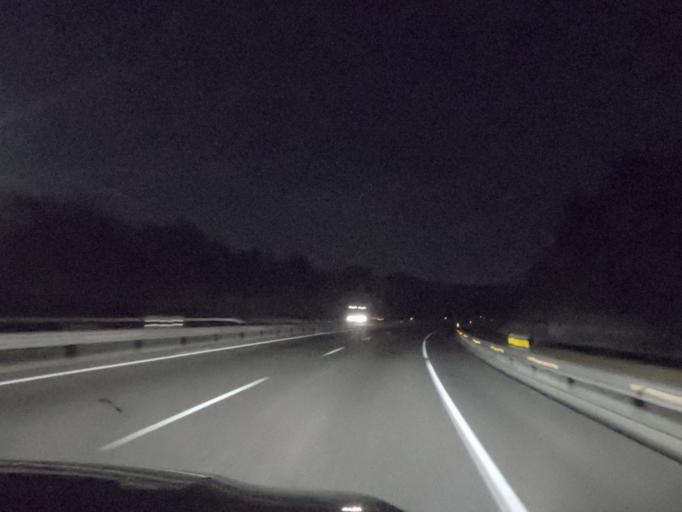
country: ES
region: Galicia
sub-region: Provincia de Ourense
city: Taboadela
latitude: 42.2351
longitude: -7.8497
